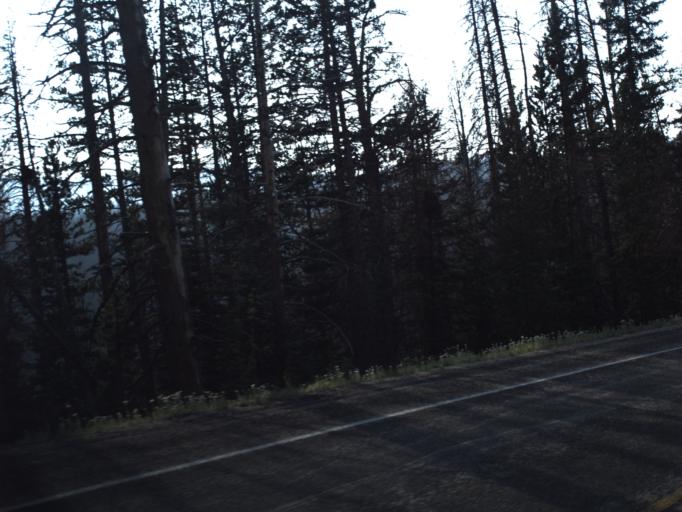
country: US
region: Utah
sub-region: Summit County
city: Kamas
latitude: 40.6755
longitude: -110.9507
